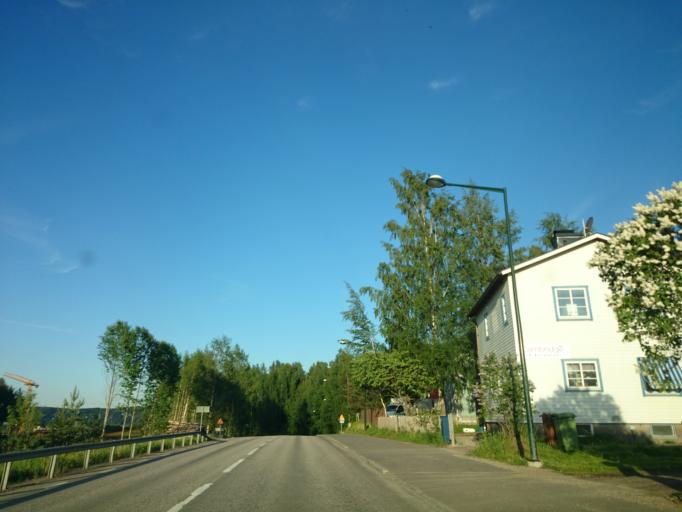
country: SE
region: Vaesternorrland
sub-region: Sundsvalls Kommun
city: Sundsvall
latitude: 62.3815
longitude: 17.3443
